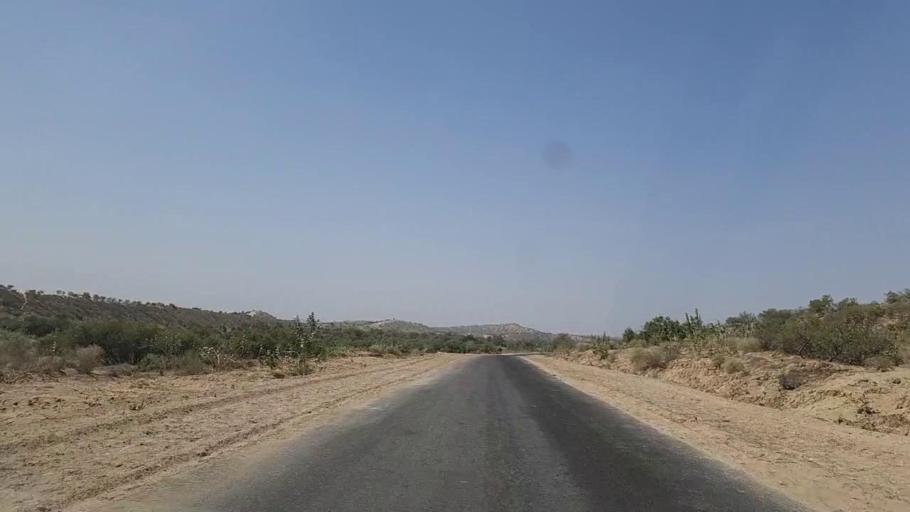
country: PK
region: Sindh
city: Diplo
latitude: 24.5794
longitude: 69.5012
